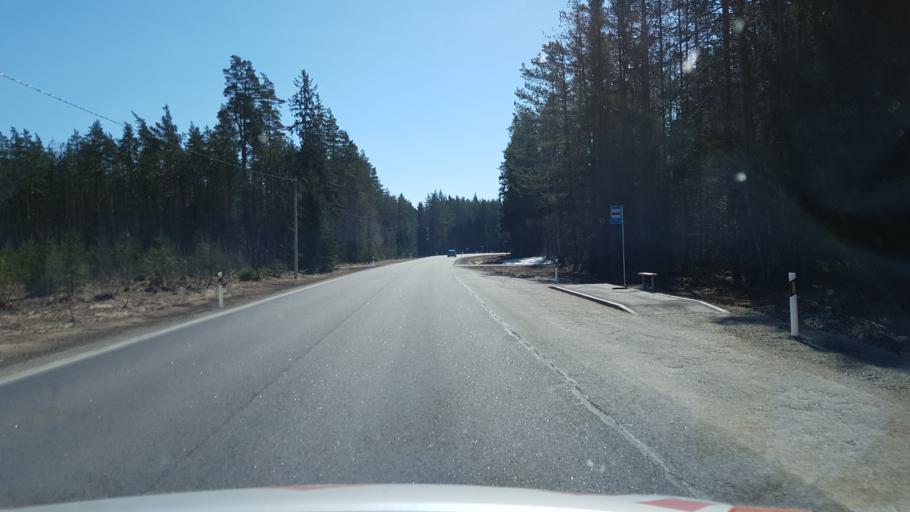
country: EE
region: Laeaene-Virumaa
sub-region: Vinni vald
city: Vinni
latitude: 59.1270
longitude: 26.6132
